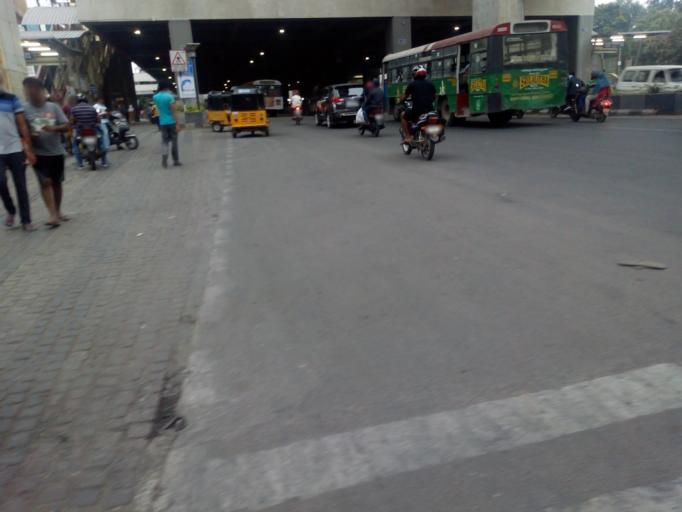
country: IN
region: Telangana
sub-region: Hyderabad
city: Hyderabad
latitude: 17.4365
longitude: 78.4442
